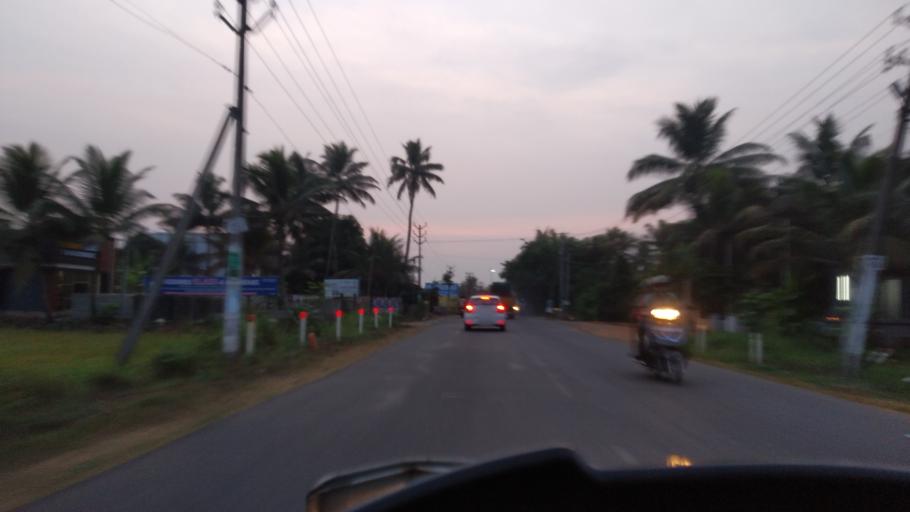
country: IN
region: Kerala
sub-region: Kottayam
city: Kottayam
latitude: 9.5922
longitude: 76.4518
